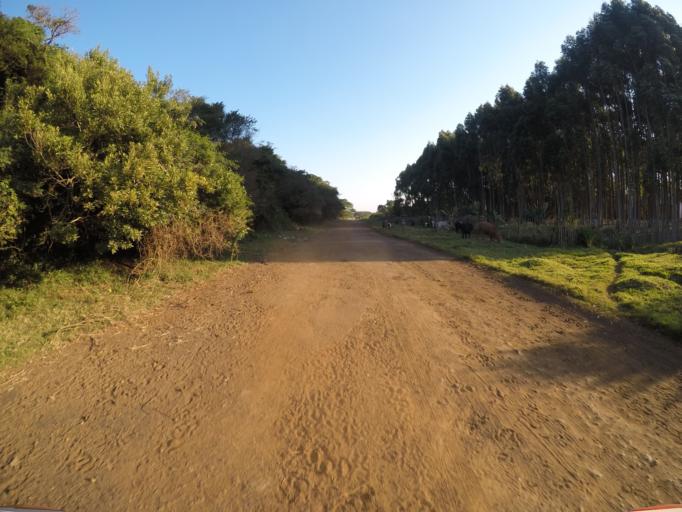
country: ZA
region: KwaZulu-Natal
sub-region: uThungulu District Municipality
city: KwaMbonambi
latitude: -28.6973
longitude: 32.1952
